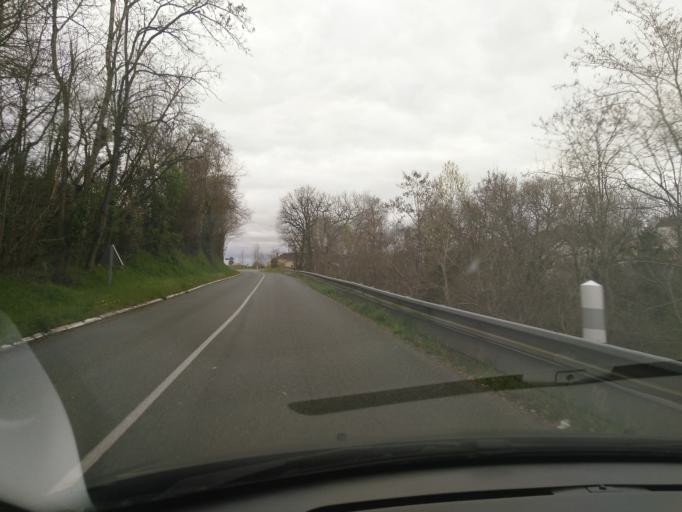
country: FR
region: Aquitaine
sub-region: Departement du Lot-et-Garonne
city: Foulayronnes
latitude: 44.2420
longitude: 0.6428
